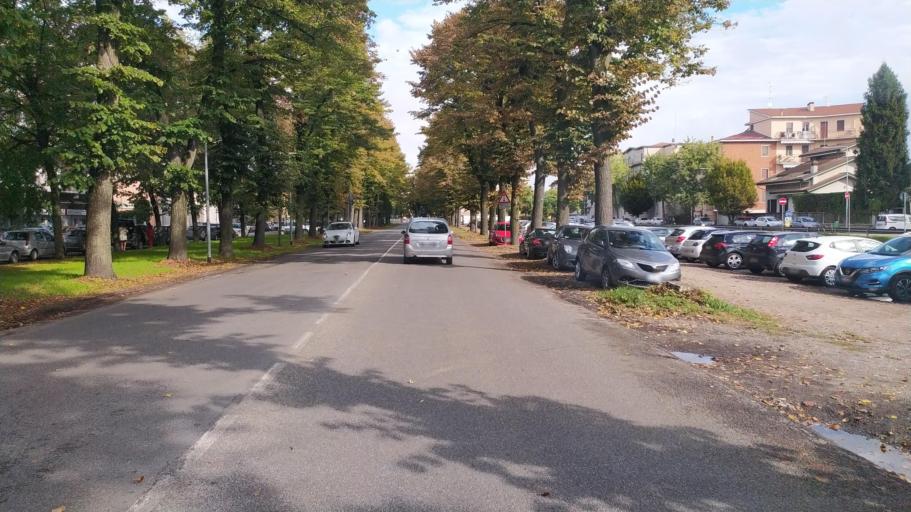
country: IT
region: Lombardy
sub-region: Provincia di Pavia
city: Pavia
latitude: 45.1952
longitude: 9.1574
